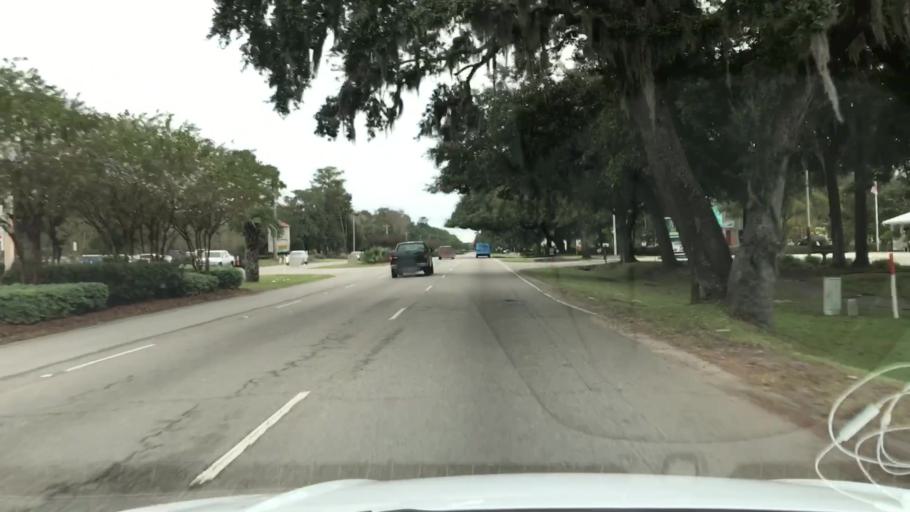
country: US
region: South Carolina
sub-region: Georgetown County
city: Murrells Inlet
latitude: 33.4867
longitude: -79.0938
